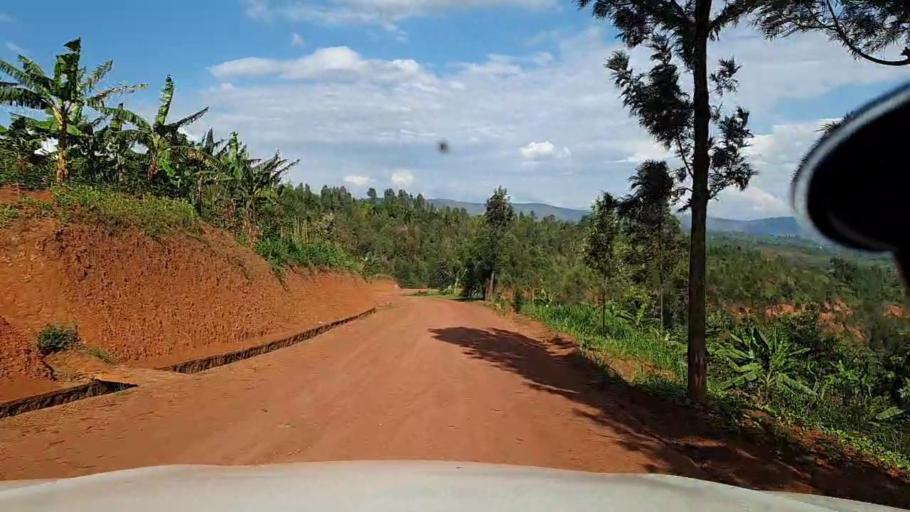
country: RW
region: Kigali
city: Kigali
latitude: -1.8397
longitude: 29.8526
